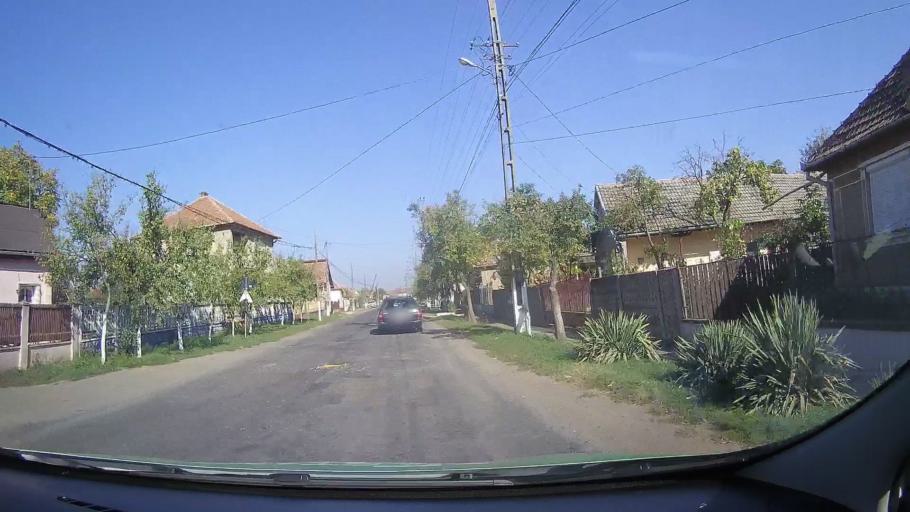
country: RO
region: Satu Mare
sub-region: Comuna Sanislau
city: Sanislau
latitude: 47.6343
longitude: 22.3265
